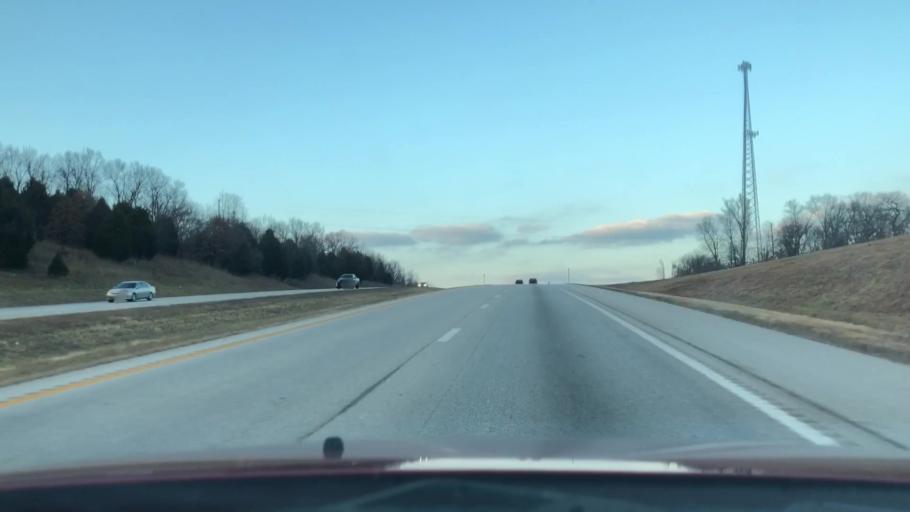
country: US
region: Missouri
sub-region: Christian County
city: Ozark
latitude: 36.9161
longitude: -93.2438
